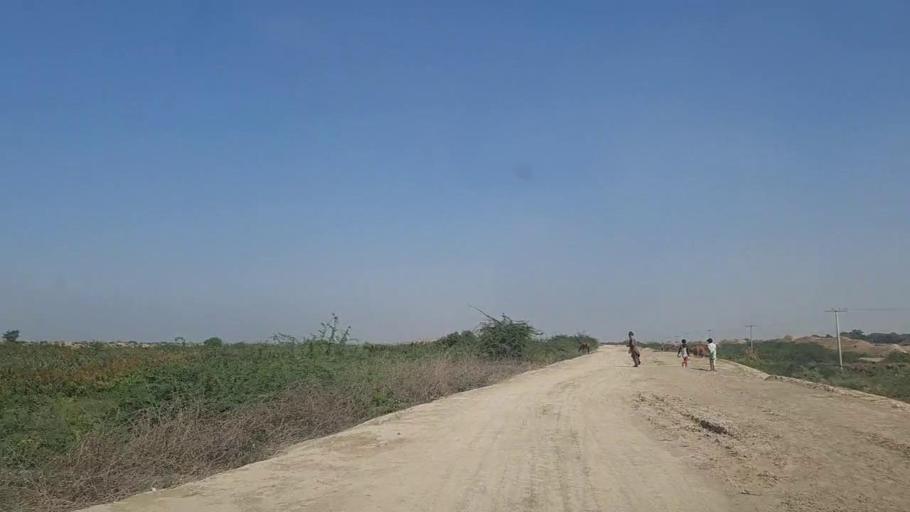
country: PK
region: Sindh
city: Thatta
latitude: 24.8546
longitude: 68.0331
